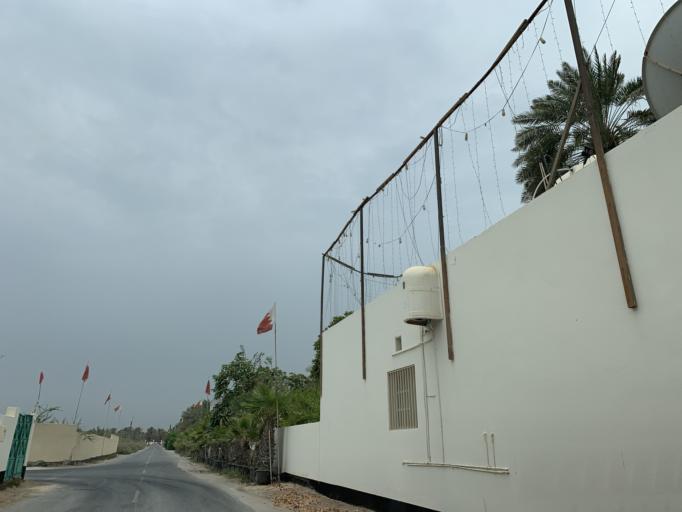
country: BH
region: Central Governorate
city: Madinat Hamad
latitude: 26.1853
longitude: 50.4686
